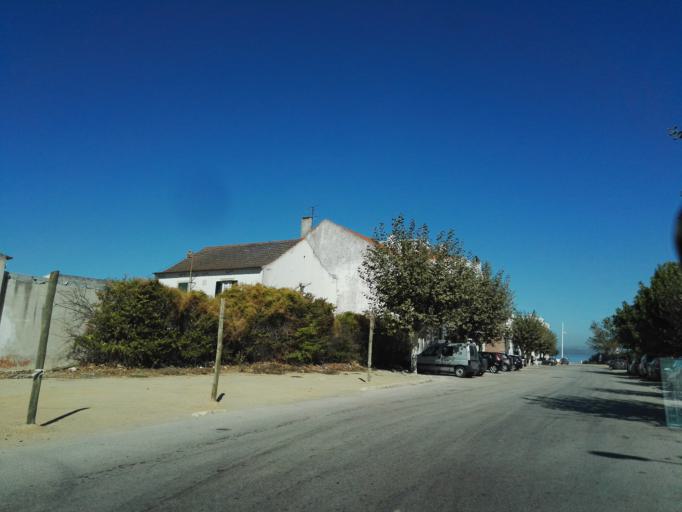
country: PT
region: Setubal
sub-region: Alcochete
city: Alcochete
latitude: 38.7561
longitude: -8.9578
